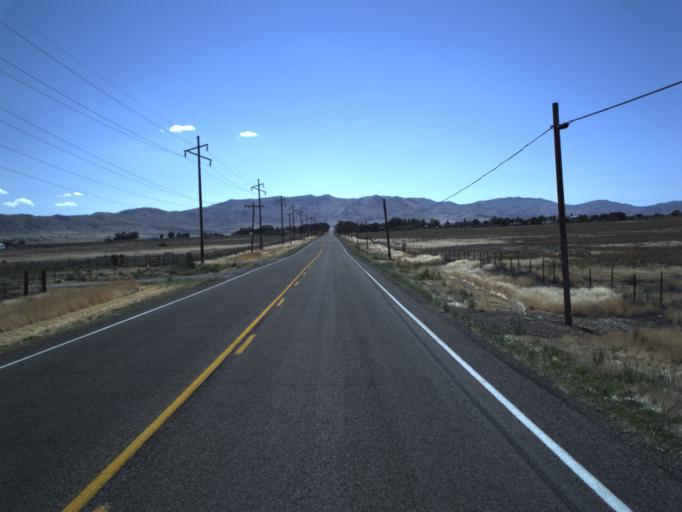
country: US
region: Utah
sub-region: Utah County
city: Genola
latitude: 39.9726
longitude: -111.9569
